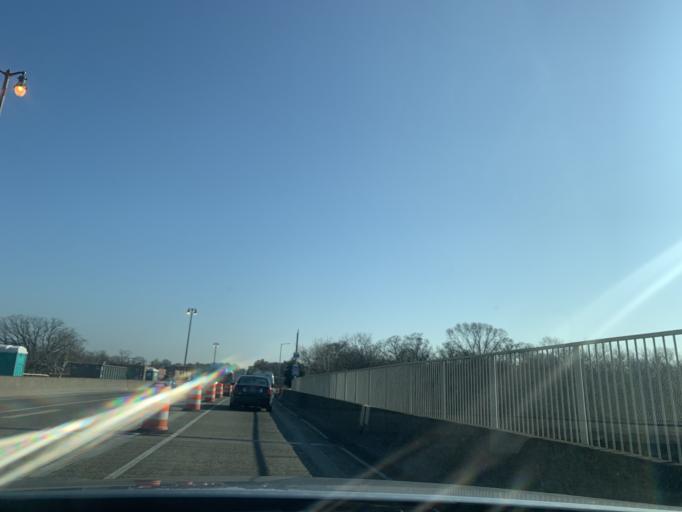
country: US
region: Maryland
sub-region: Prince George's County
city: Coral Hills
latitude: 38.8900
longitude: -76.9634
